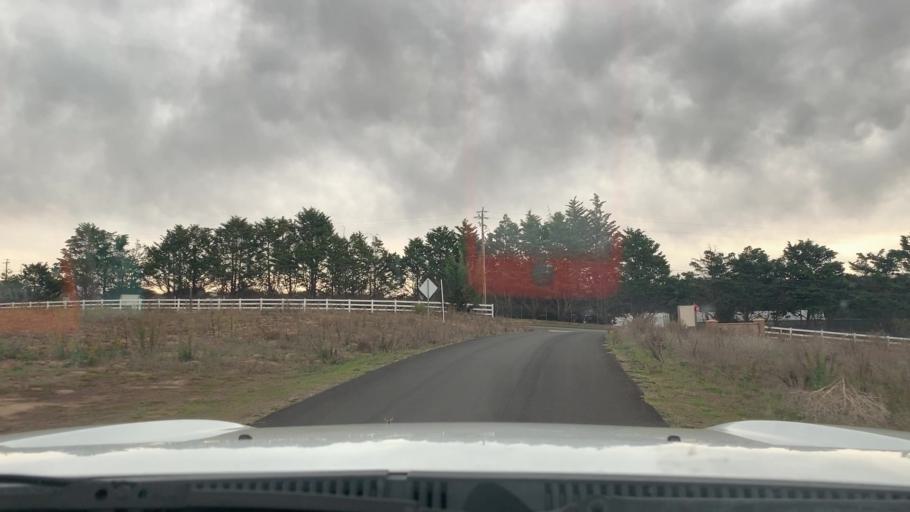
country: US
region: California
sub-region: San Luis Obispo County
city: Callender
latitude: 35.0655
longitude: -120.5617
